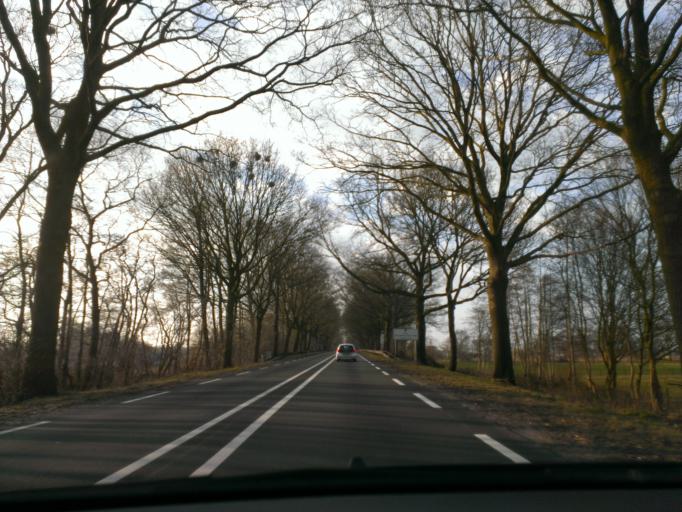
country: NL
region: Overijssel
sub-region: Gemeente Raalte
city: Raalte
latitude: 52.3884
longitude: 6.2870
